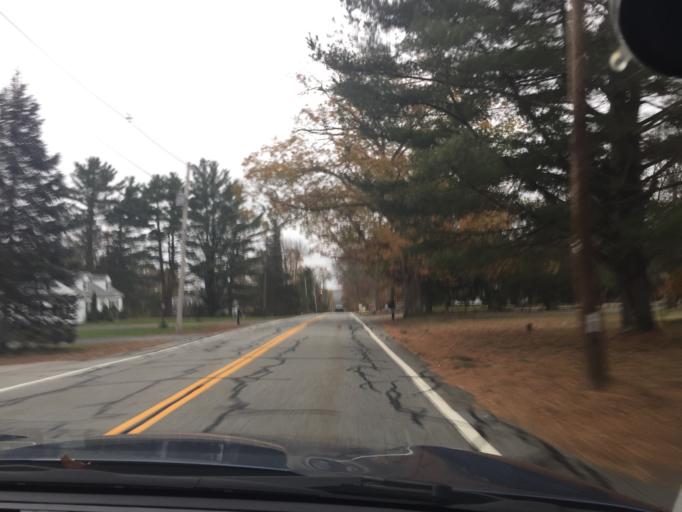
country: US
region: Rhode Island
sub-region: Providence County
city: North Scituate
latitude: 41.8101
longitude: -71.6602
